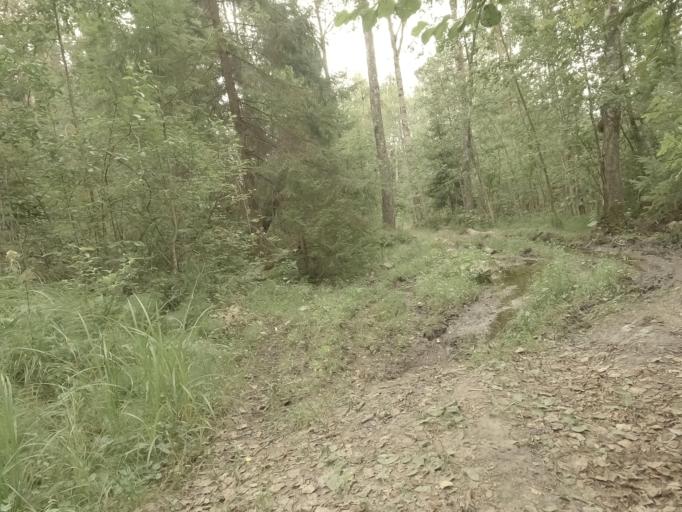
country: RU
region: Leningrad
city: Kamennogorsk
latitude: 61.0757
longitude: 29.1576
